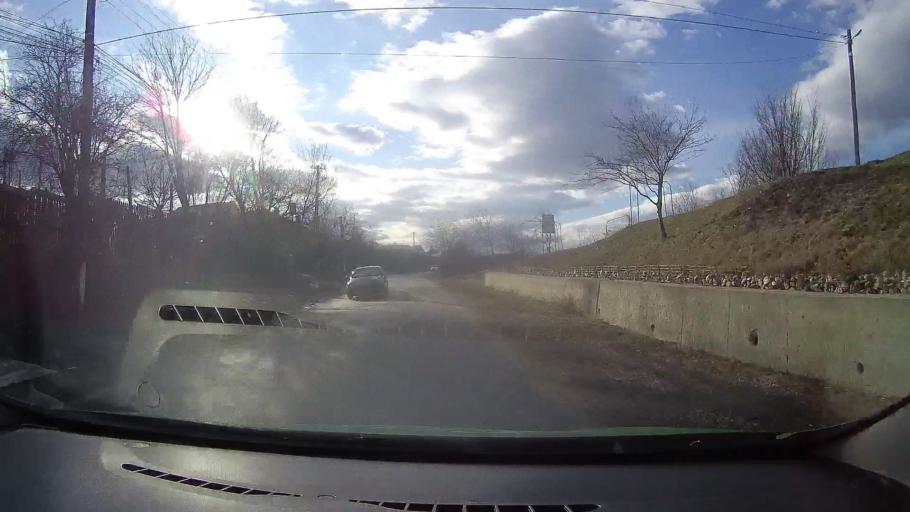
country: RO
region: Dambovita
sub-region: Comuna Ulmi
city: Ulmi
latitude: 44.8885
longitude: 25.5082
